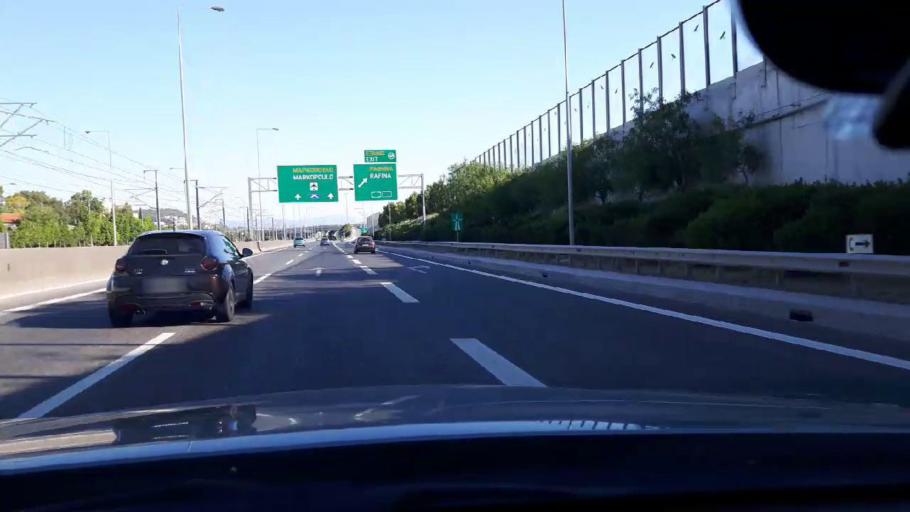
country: GR
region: Attica
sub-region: Nomarchia Anatolikis Attikis
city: Pallini
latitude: 37.9890
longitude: 23.8713
